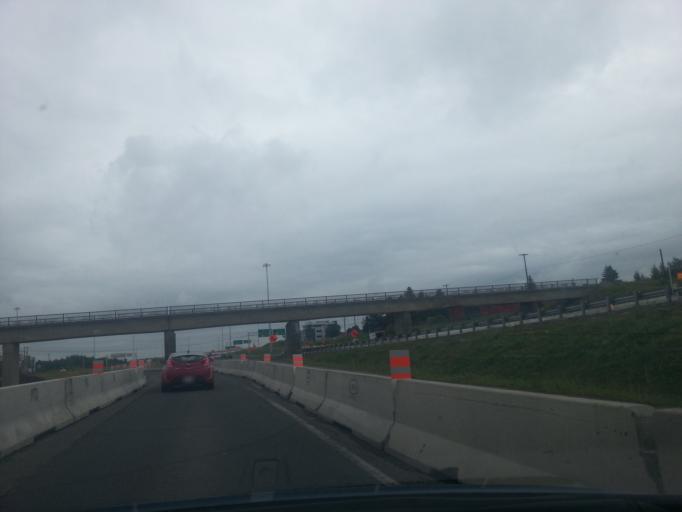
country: CA
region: Quebec
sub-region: Chaudiere-Appalaches
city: Breakeyville
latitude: 46.7226
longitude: -71.2828
